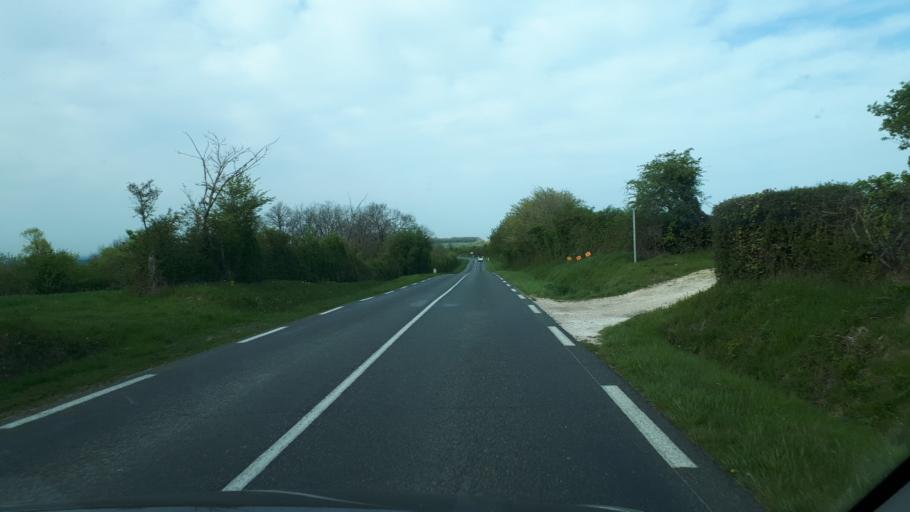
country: FR
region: Centre
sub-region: Departement du Cher
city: Rians
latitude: 47.2395
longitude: 2.6536
